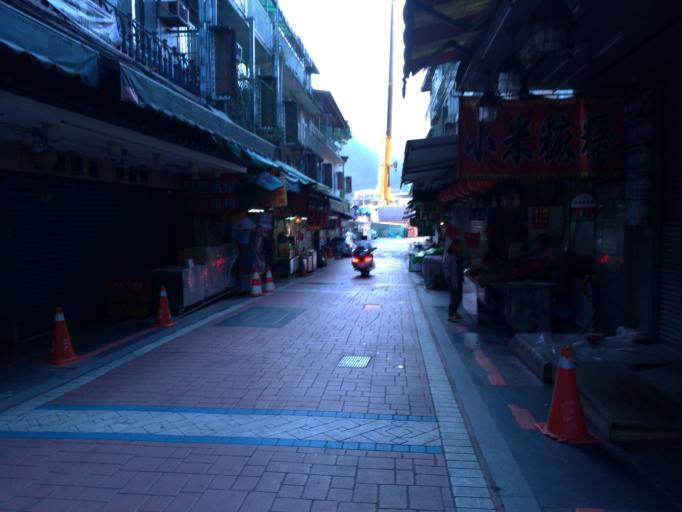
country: TW
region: Taipei
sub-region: Taipei
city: Banqiao
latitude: 24.8630
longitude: 121.5515
